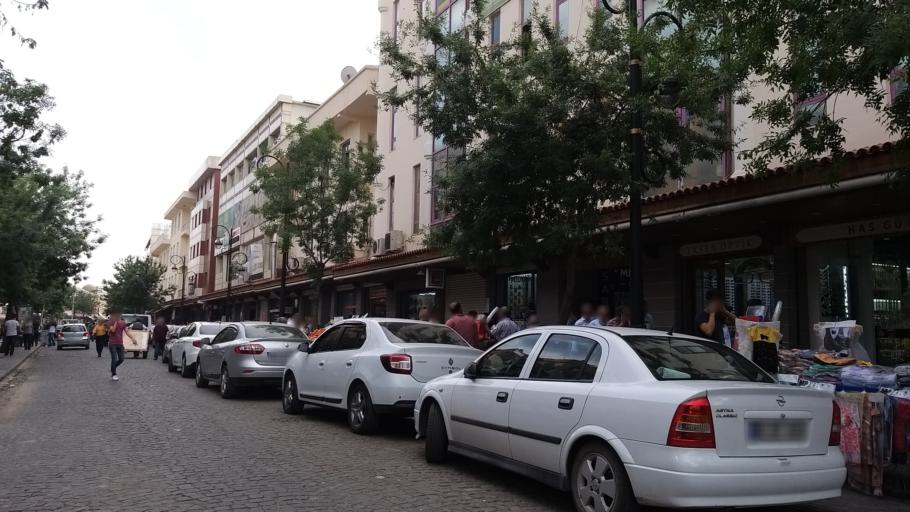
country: TR
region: Diyarbakir
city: Sur
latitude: 37.9148
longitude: 40.2369
